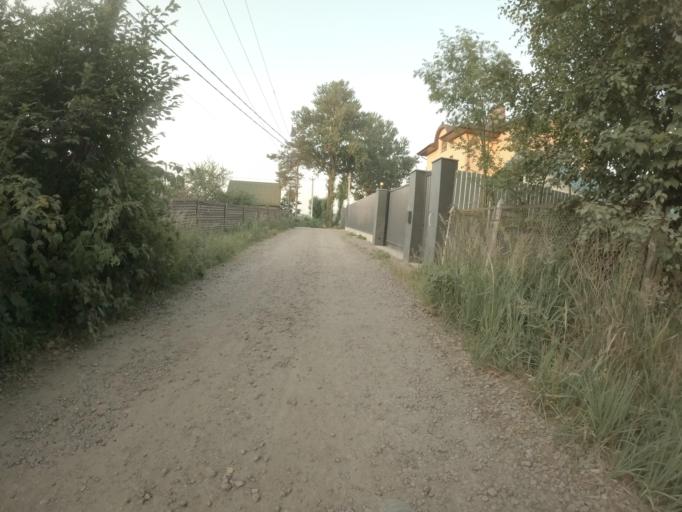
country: RU
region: Leningrad
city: Imeni Sverdlova
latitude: 59.7855
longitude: 30.7159
